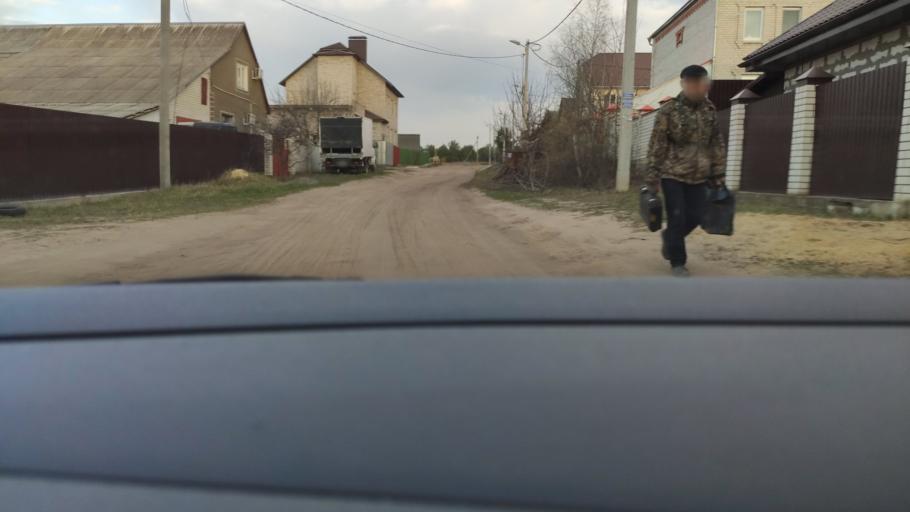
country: RU
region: Voronezj
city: Pridonskoy
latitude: 51.6294
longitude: 39.0925
